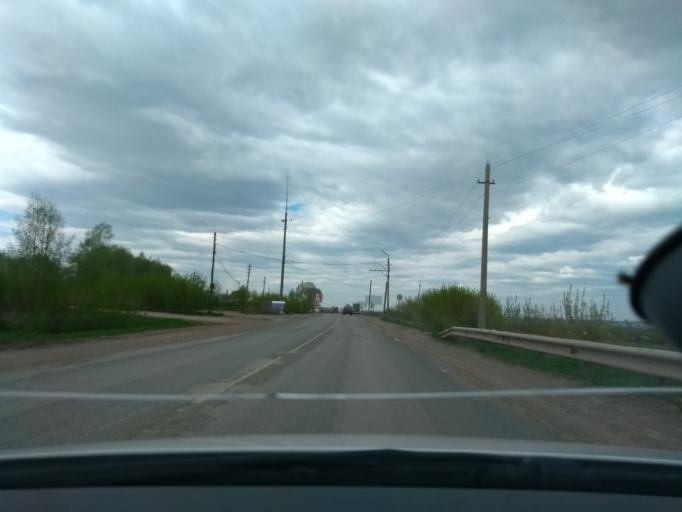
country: RU
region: Perm
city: Lobanovo
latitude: 57.8641
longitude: 56.2942
